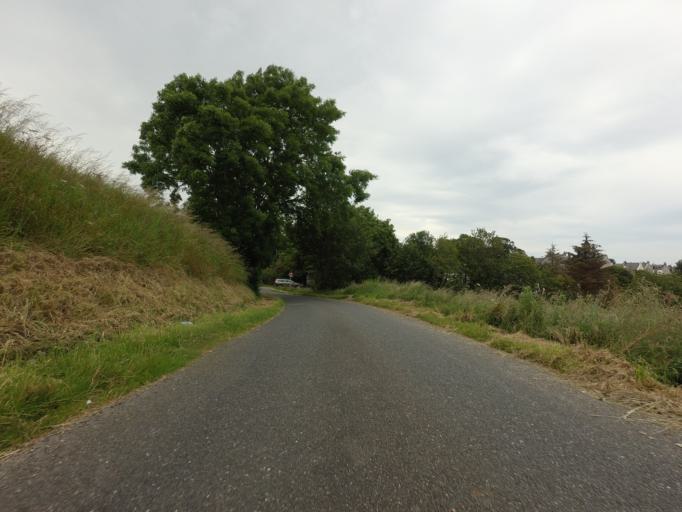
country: GB
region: Scotland
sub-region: Aberdeenshire
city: Portsoy
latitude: 57.6784
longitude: -2.6865
